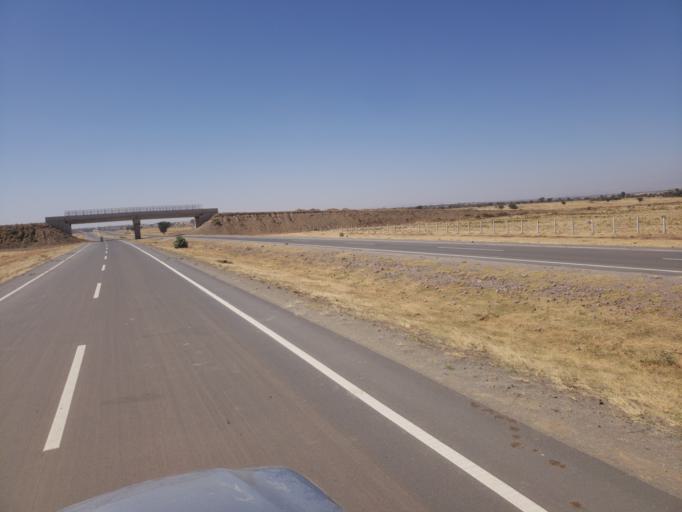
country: ET
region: Oromiya
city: Ziway
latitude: 8.2456
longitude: 38.8844
